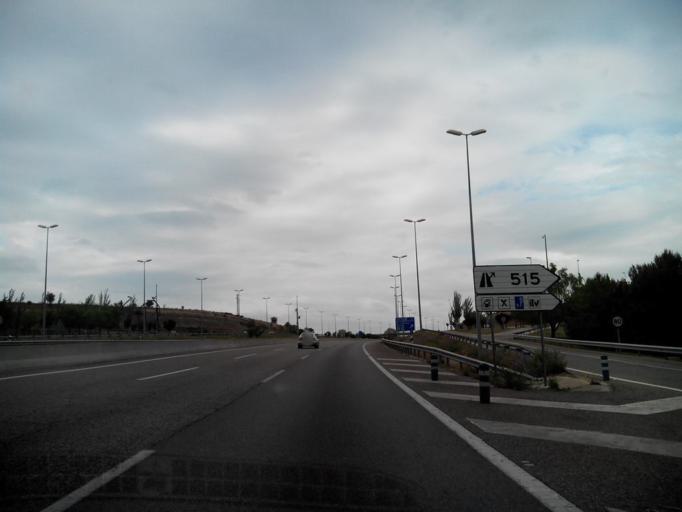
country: ES
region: Catalonia
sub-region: Provincia de Lleida
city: Cervera
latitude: 41.6715
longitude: 1.2238
